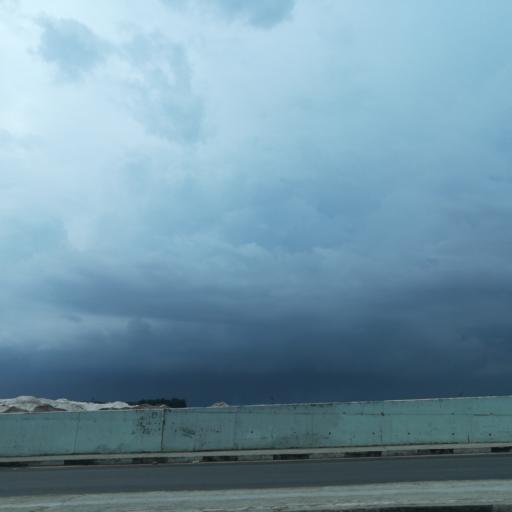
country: NG
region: Rivers
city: Port Harcourt
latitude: 4.8051
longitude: 7.0592
